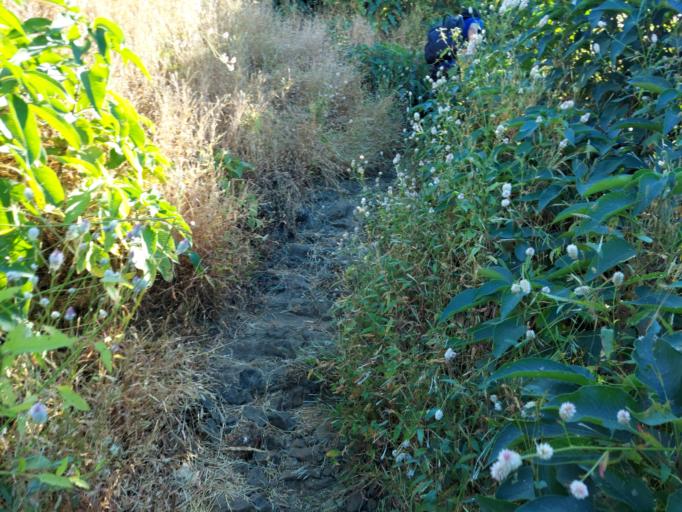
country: IN
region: Maharashtra
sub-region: Sindhudurg
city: Kudal
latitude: 16.0862
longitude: 73.8427
